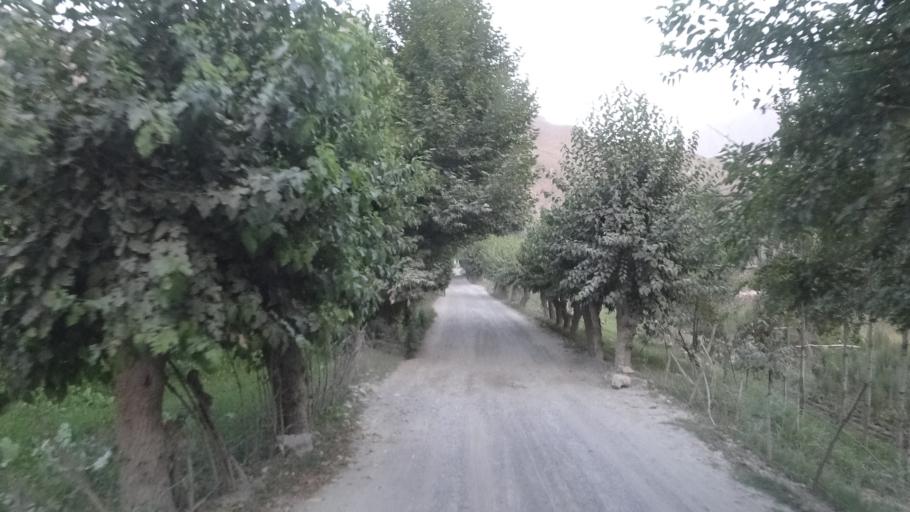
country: AF
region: Badakhshan
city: Maymay
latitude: 38.4230
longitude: 71.1056
